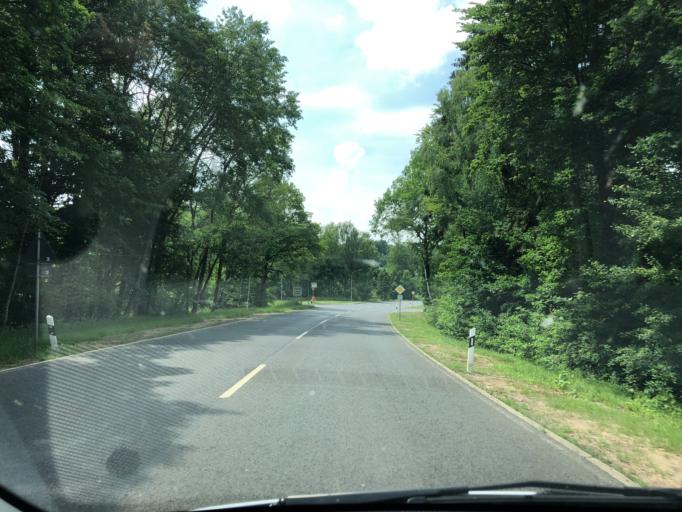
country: DE
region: Hesse
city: Stadtallendorf
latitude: 50.8263
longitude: 9.0387
